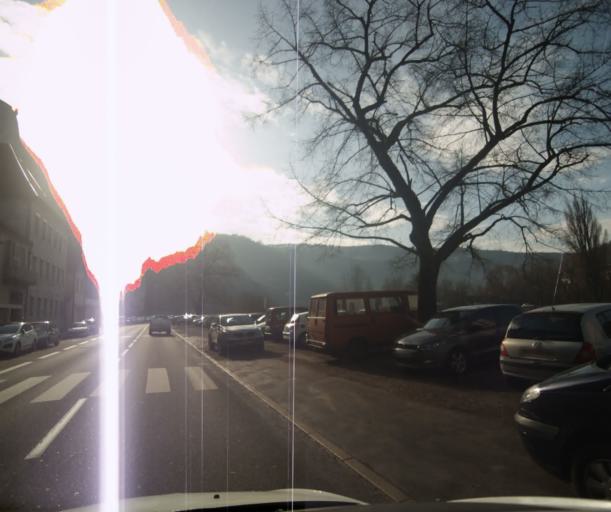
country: FR
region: Franche-Comte
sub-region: Departement du Doubs
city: Besancon
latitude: 47.2285
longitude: 6.0318
